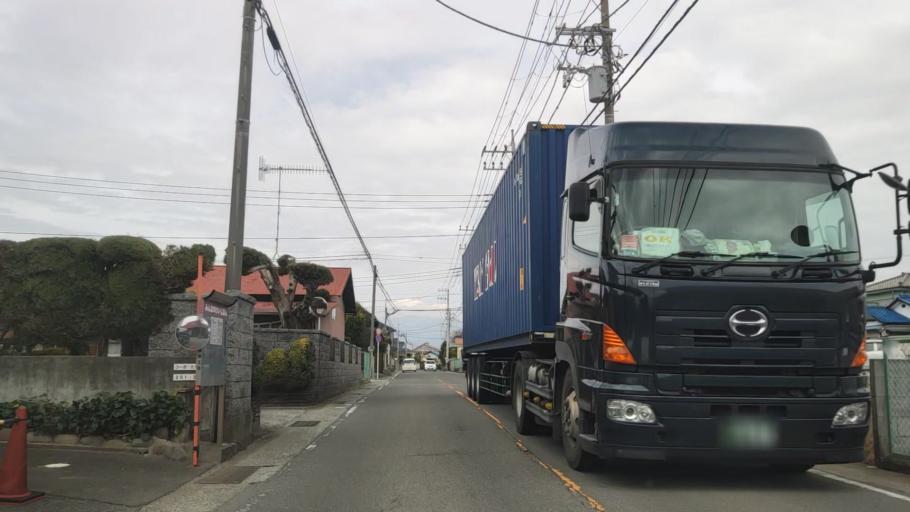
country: JP
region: Kanagawa
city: Ninomiya
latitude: 35.2942
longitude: 139.2335
